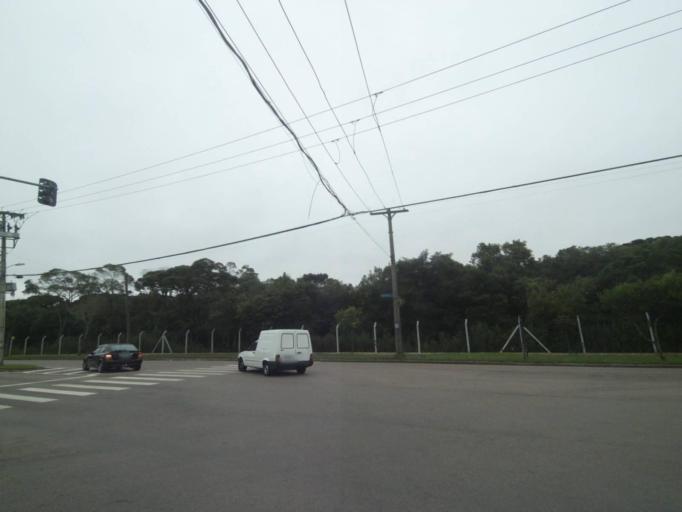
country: BR
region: Parana
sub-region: Sao Jose Dos Pinhais
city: Sao Jose dos Pinhais
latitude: -25.5287
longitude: -49.3131
